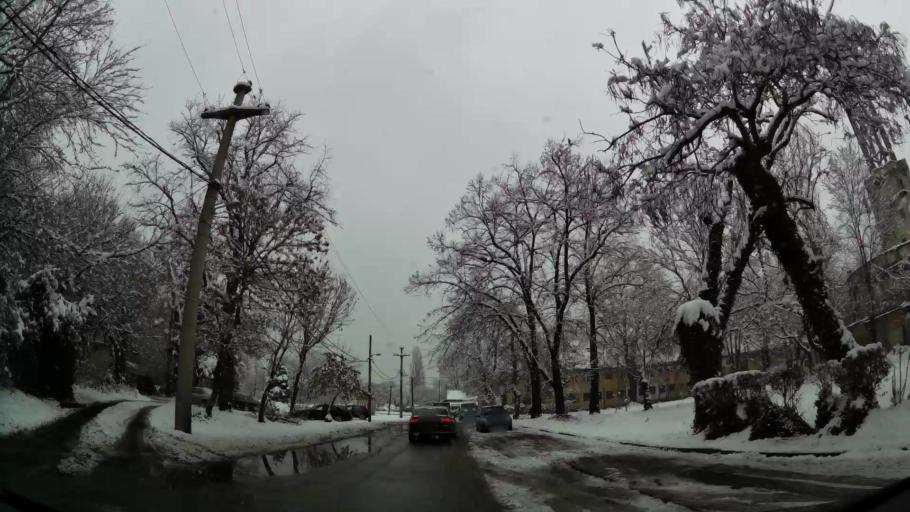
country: RS
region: Central Serbia
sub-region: Belgrade
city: Novi Beograd
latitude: 44.8133
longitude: 20.4420
